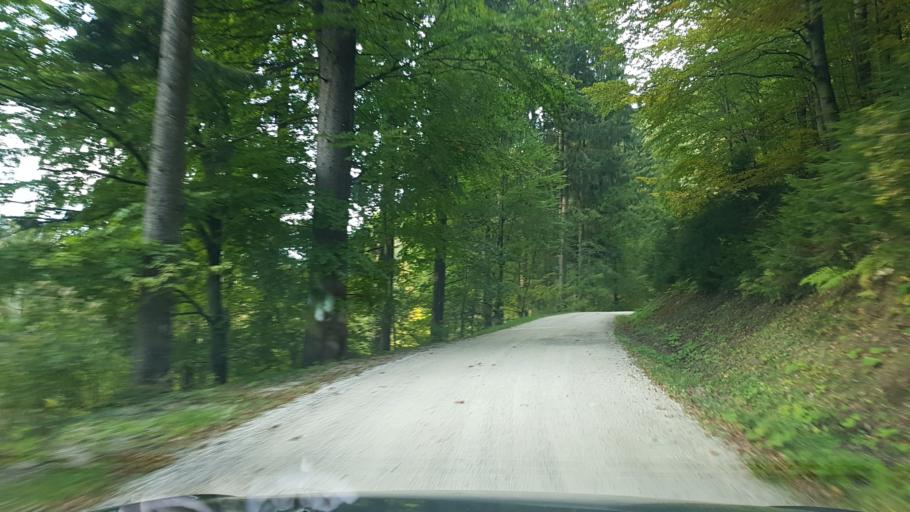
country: SI
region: Slovenj Gradec
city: Legen
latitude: 46.5237
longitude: 15.1280
